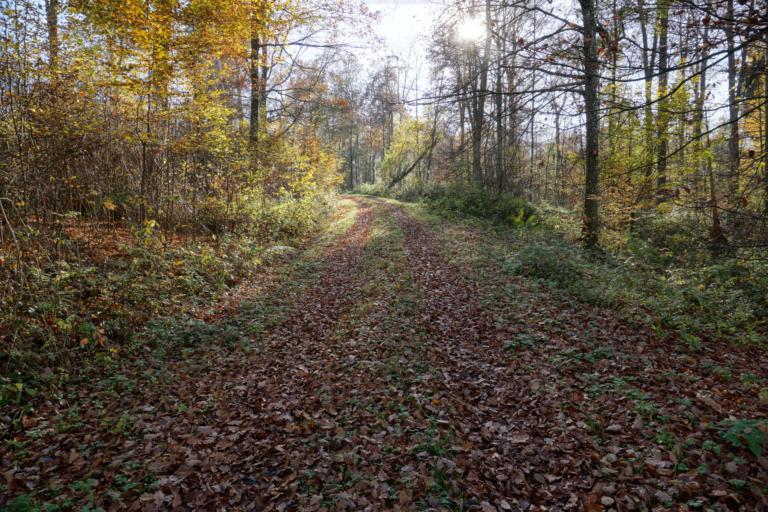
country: DE
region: Baden-Wuerttemberg
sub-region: Karlsruhe Region
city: Aglasterhausen
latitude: 49.3672
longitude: 8.9972
